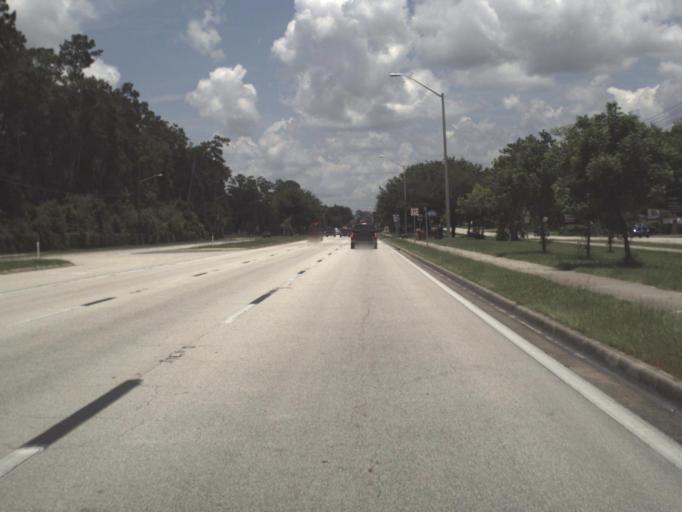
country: US
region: Florida
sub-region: Alachua County
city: Gainesville
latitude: 29.6299
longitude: -82.3664
